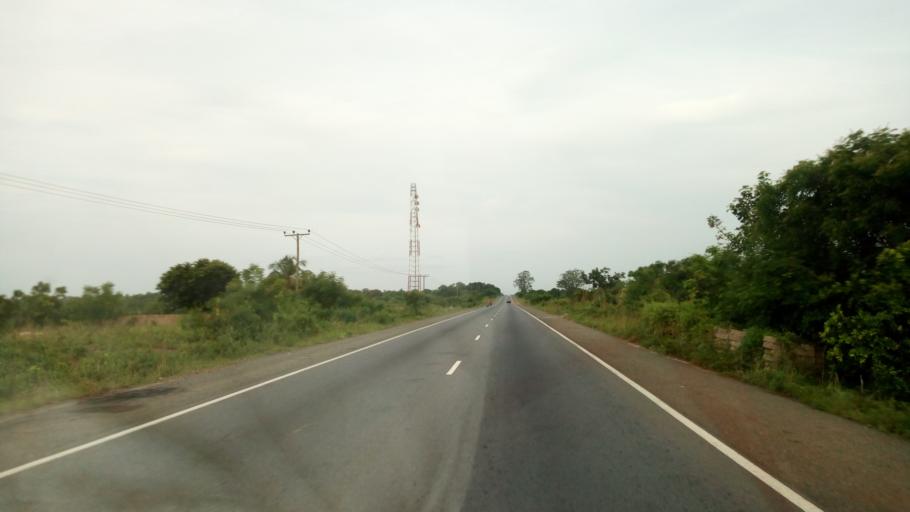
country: GH
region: Volta
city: Keta
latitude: 6.0636
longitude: 1.0059
